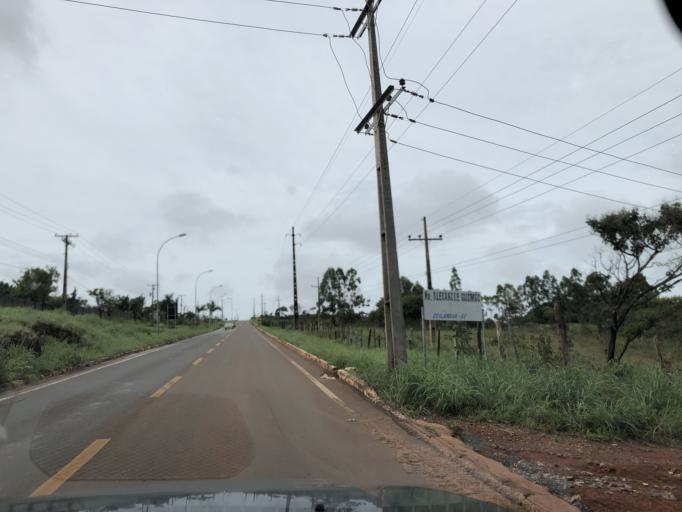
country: BR
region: Federal District
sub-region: Brasilia
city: Brasilia
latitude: -15.7724
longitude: -48.1289
